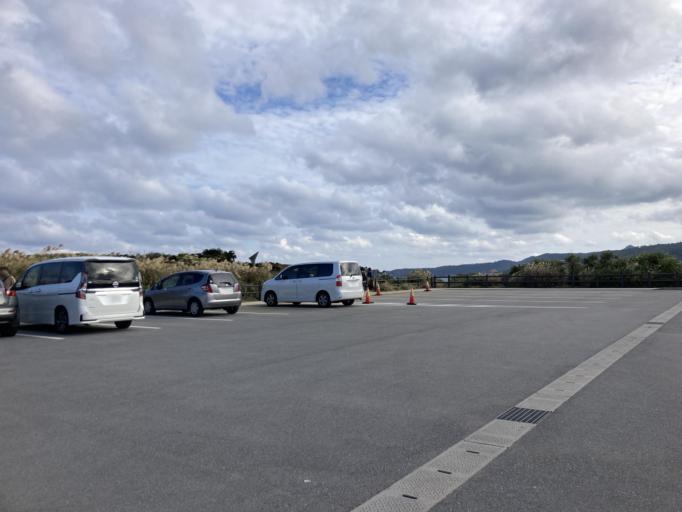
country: JP
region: Okinawa
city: Nago
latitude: 26.8724
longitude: 128.2638
